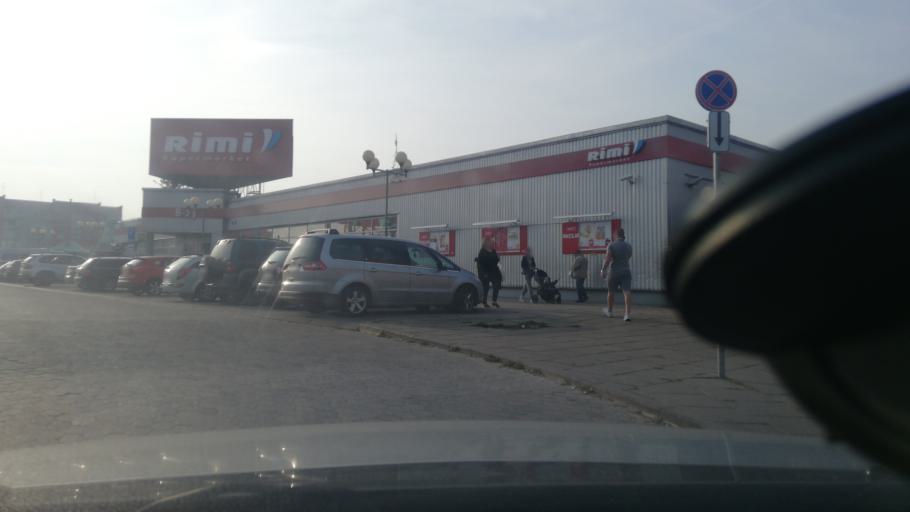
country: LT
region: Klaipedos apskritis
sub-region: Klaipeda
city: Klaipeda
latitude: 55.6674
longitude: 21.1977
